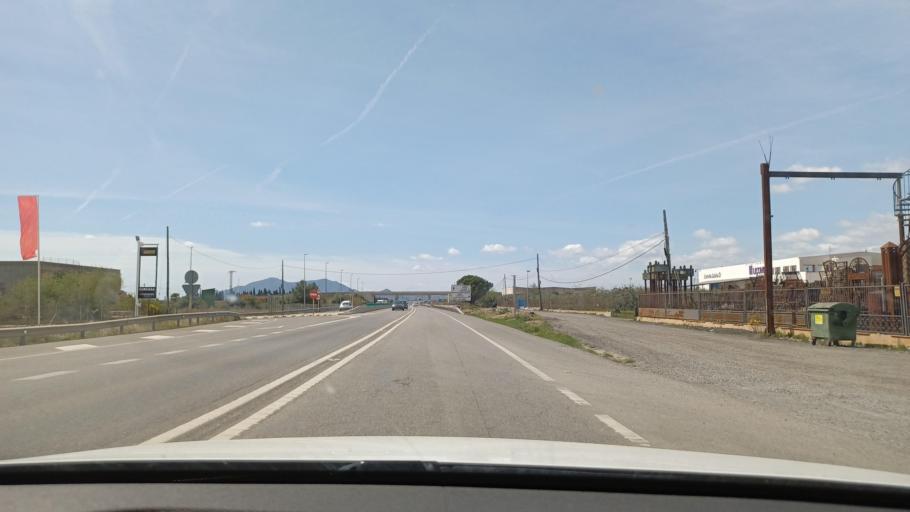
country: ES
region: Catalonia
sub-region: Provincia de Tarragona
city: Camarles
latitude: 40.7672
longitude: 0.6477
